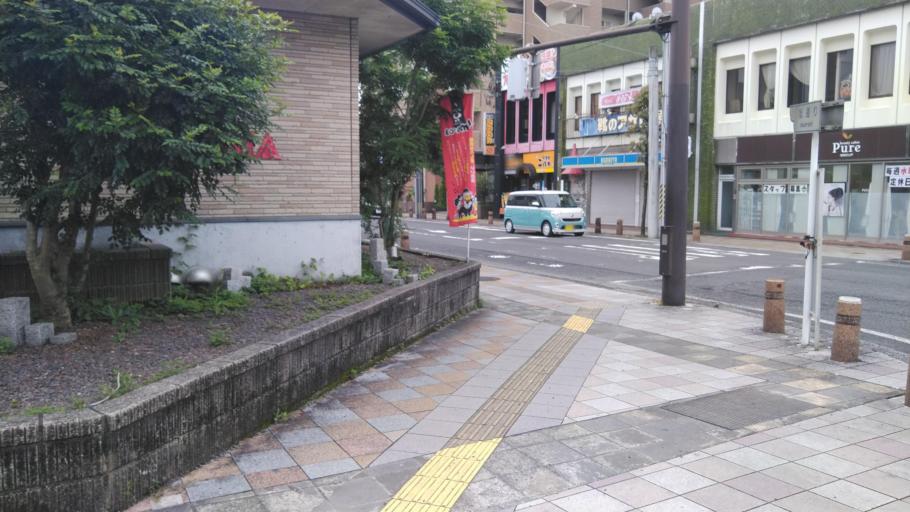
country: JP
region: Kagoshima
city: Kokubu-matsuki
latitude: 31.7407
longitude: 130.7675
